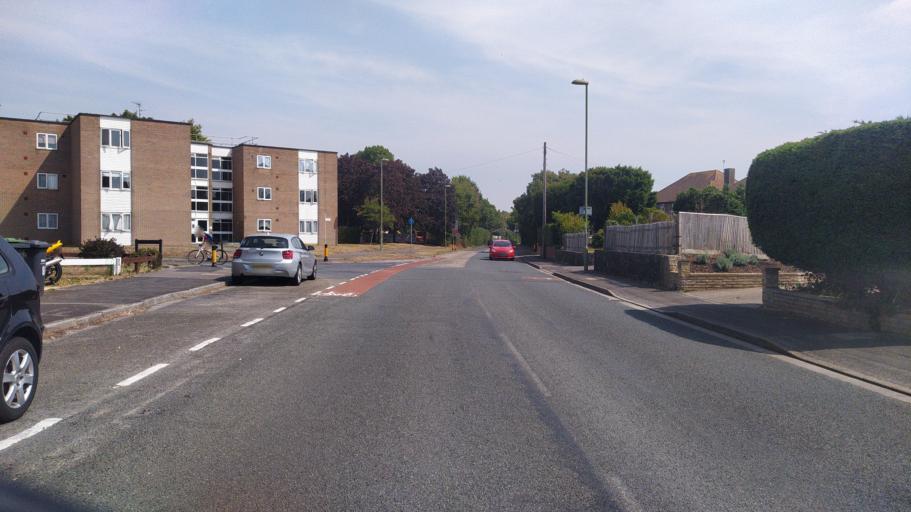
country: GB
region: England
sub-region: Hampshire
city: Havant
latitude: 50.8600
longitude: -0.9622
